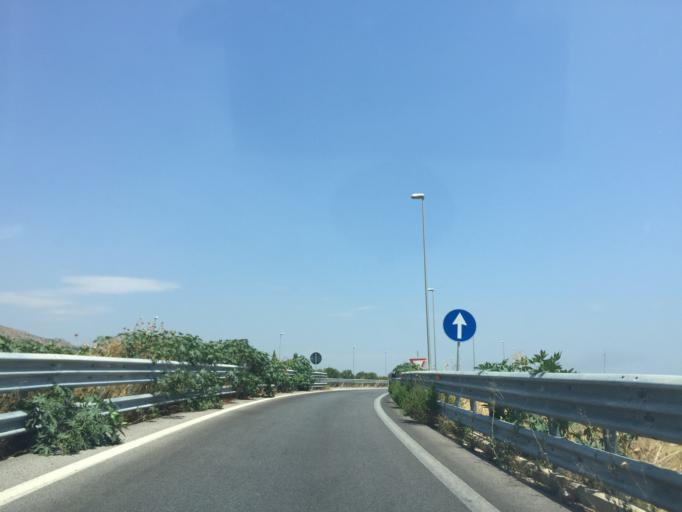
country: IT
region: Sicily
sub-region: Provincia di Siracusa
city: Avola
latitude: 36.9366
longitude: 15.1553
